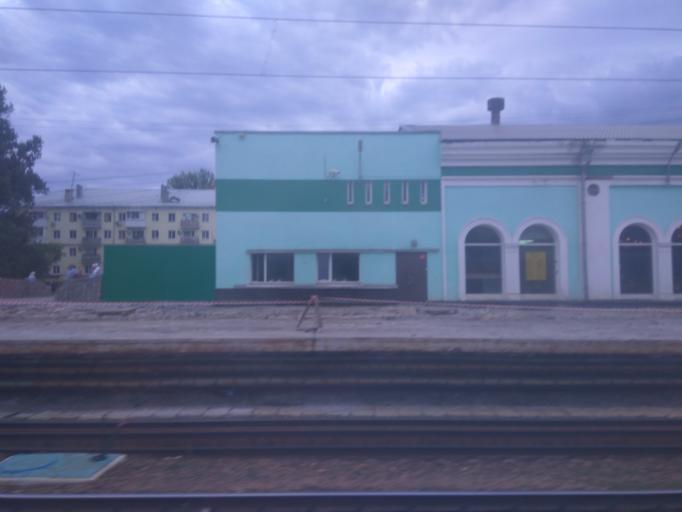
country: RU
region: Saratov
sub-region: Saratovskiy Rayon
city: Saratov
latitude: 51.5424
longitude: 45.9990
